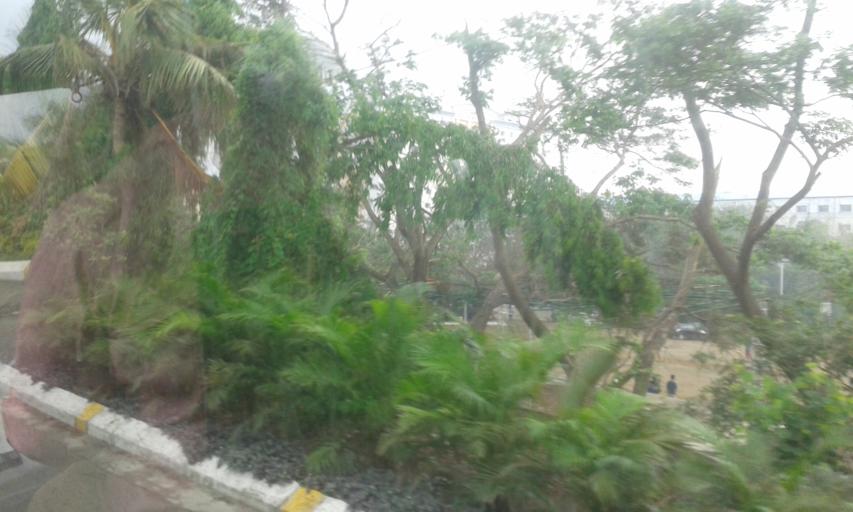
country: IN
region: Tamil Nadu
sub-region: Kancheepuram
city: Guduvancheri
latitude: 12.8247
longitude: 80.0412
